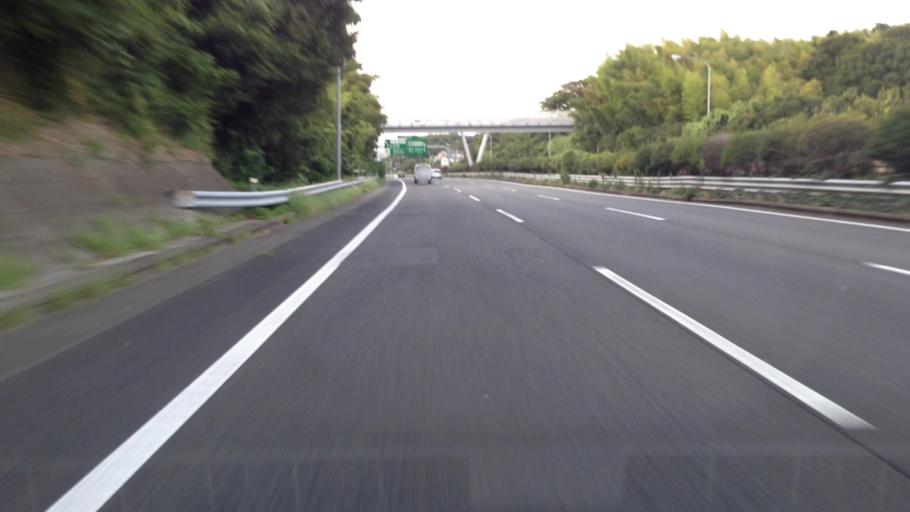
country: JP
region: Kanagawa
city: Yokohama
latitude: 35.5050
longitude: 139.5925
